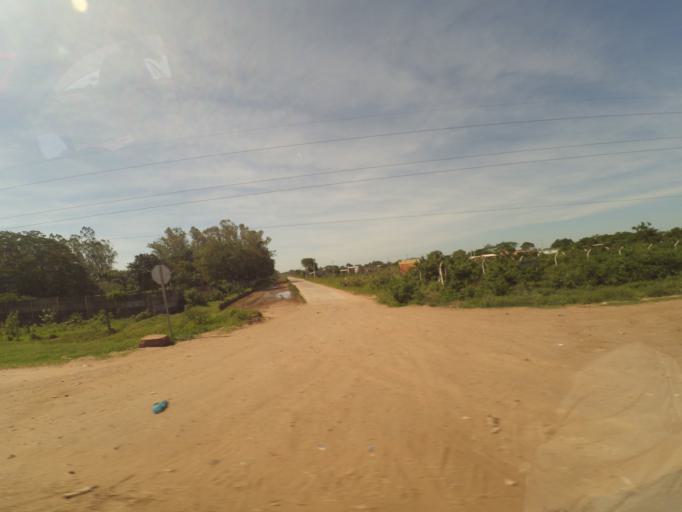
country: BO
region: Santa Cruz
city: San Julian
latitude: -17.7470
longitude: -62.9625
